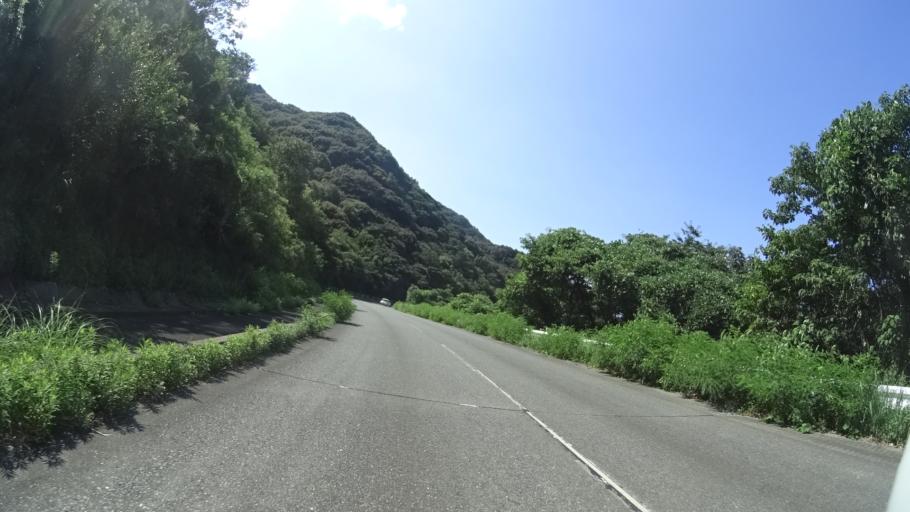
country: JP
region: Yamaguchi
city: Shimonoseki
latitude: 34.0961
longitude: 130.8892
